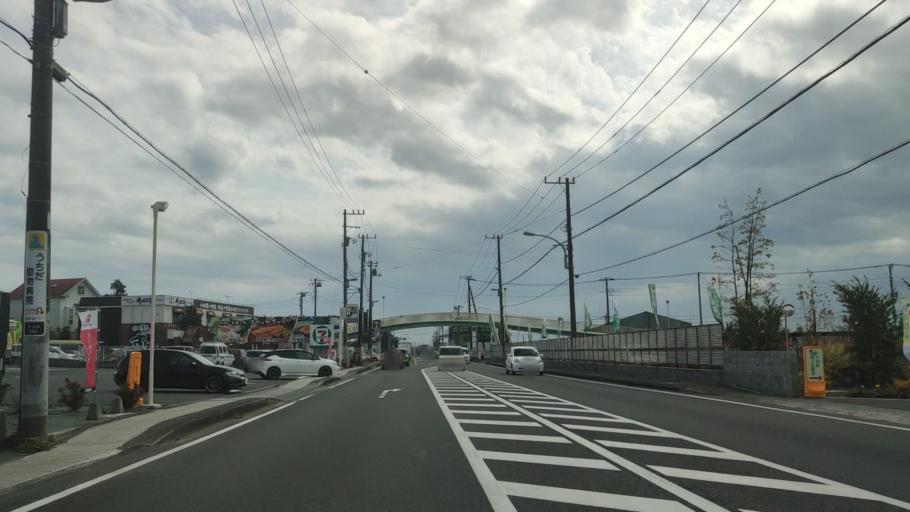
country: JP
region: Kanagawa
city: Odawara
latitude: 35.3104
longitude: 139.1635
